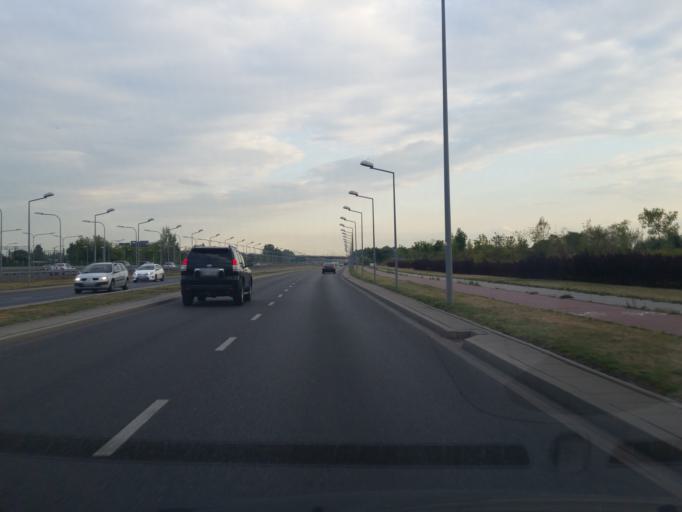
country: PL
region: Masovian Voivodeship
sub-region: Warszawa
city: Wlochy
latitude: 52.1639
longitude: 20.9858
